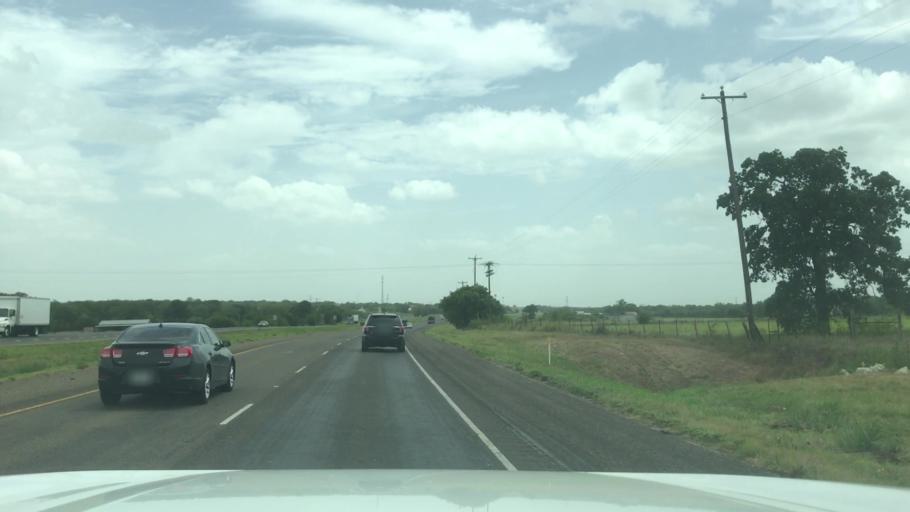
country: US
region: Texas
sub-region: McLennan County
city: Riesel
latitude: 31.4881
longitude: -96.9279
